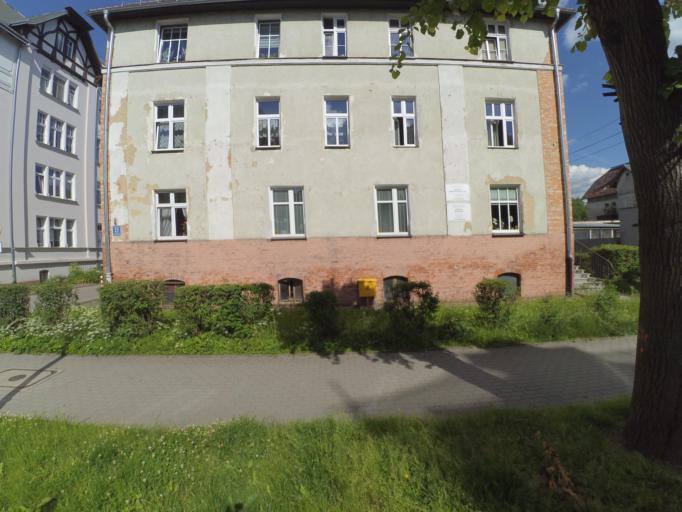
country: PL
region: Lower Silesian Voivodeship
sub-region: Powiat klodzki
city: Klodzko
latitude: 50.4325
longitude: 16.6508
